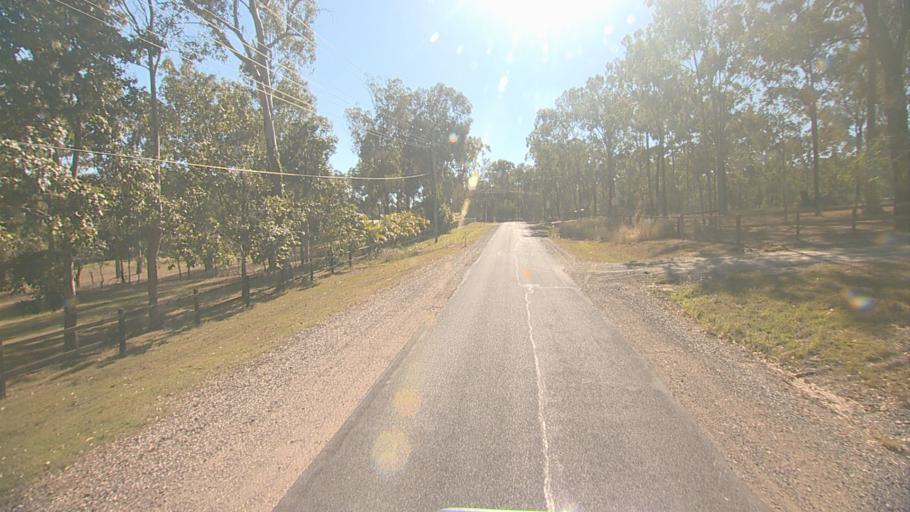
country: AU
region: Queensland
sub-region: Logan
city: Chambers Flat
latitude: -27.7723
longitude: 153.1419
